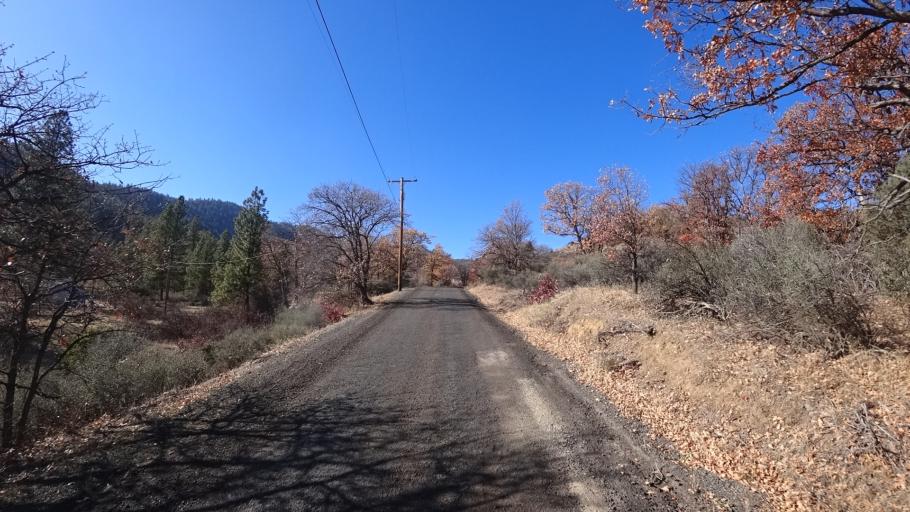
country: US
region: California
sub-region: Siskiyou County
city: Yreka
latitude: 41.7742
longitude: -122.6489
